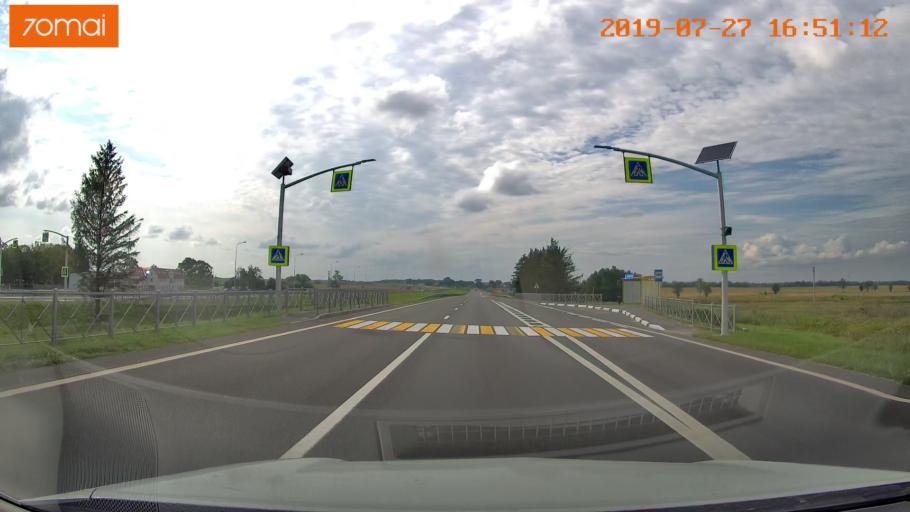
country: RU
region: Kaliningrad
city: Gvardeysk
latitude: 54.6814
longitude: 20.8934
